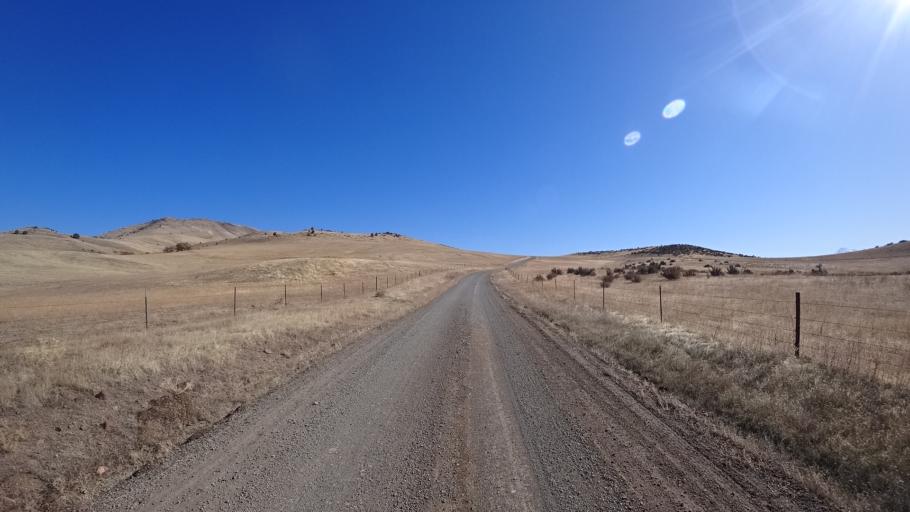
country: US
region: California
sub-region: Siskiyou County
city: Montague
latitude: 41.8464
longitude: -122.4344
